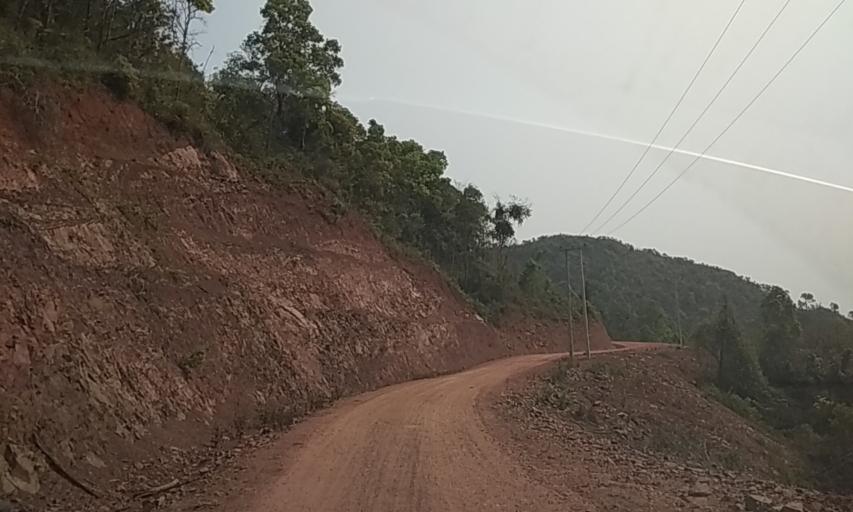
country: VN
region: Huyen Dien Bien
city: Dien Bien Phu
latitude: 21.4572
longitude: 102.7701
